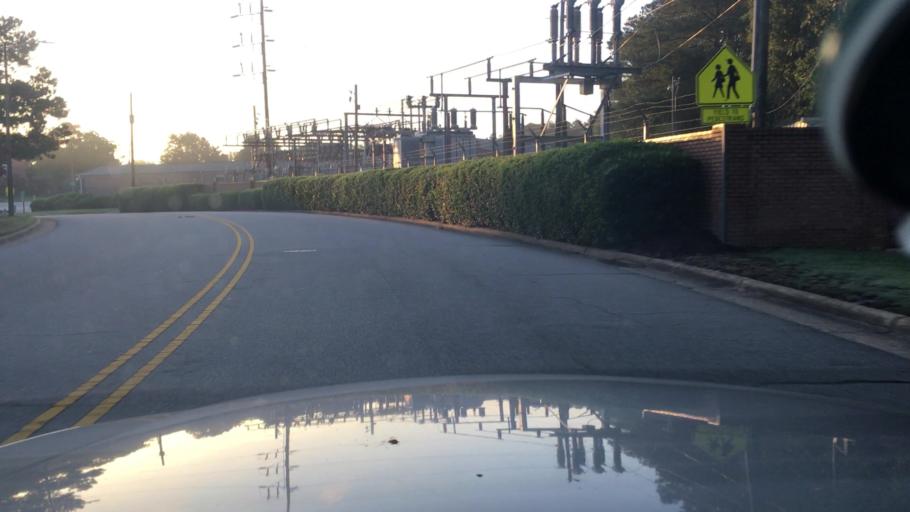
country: US
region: North Carolina
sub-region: Cumberland County
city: Fayetteville
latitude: 35.0657
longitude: -78.9259
